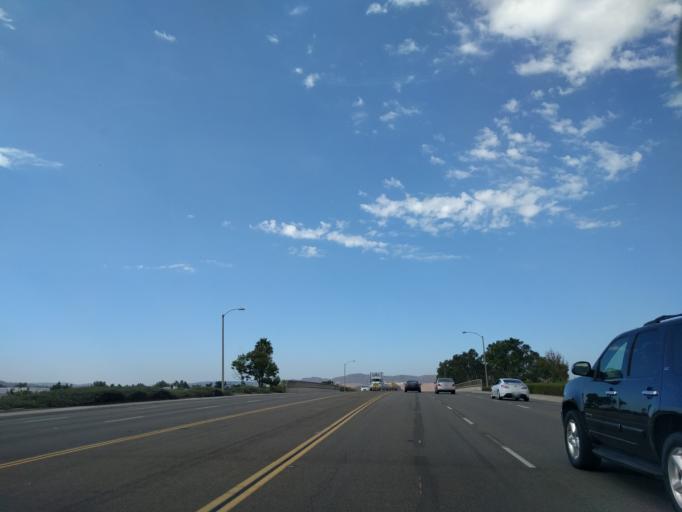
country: US
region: California
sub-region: Orange County
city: Lake Forest
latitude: 33.6501
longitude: -117.7209
